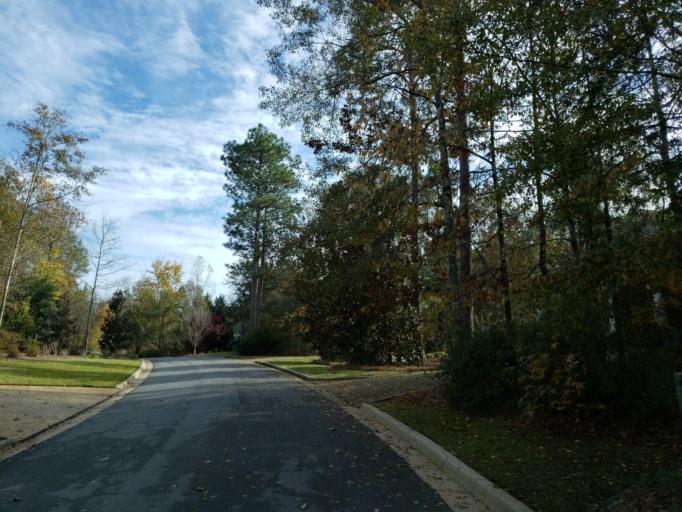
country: US
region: Mississippi
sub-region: Lamar County
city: West Hattiesburg
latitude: 31.3216
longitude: -89.4742
